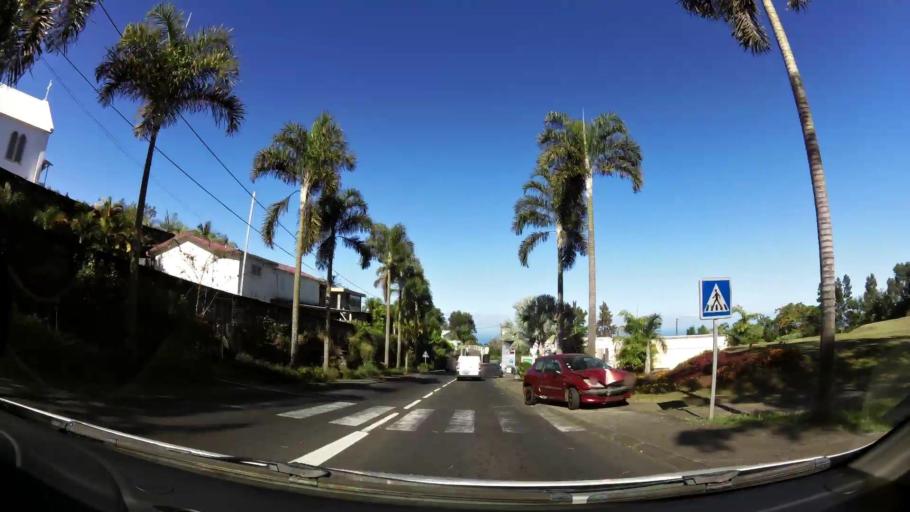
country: RE
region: Reunion
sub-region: Reunion
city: Le Tampon
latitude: -21.2553
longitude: 55.5228
